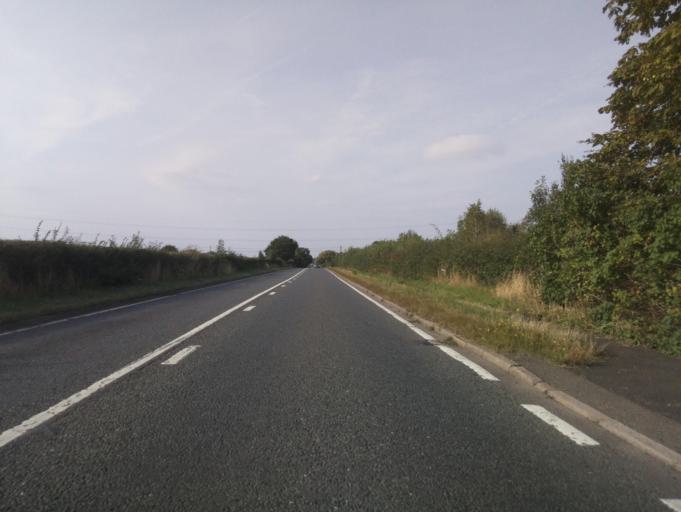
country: GB
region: England
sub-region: Warwickshire
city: Studley
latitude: 52.2517
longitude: -1.8874
